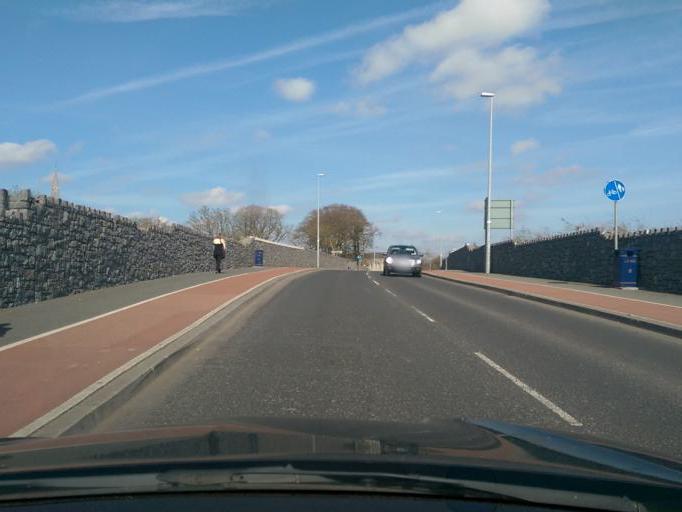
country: IE
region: Leinster
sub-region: Kildare
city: Maynooth
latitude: 53.3759
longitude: -6.5967
